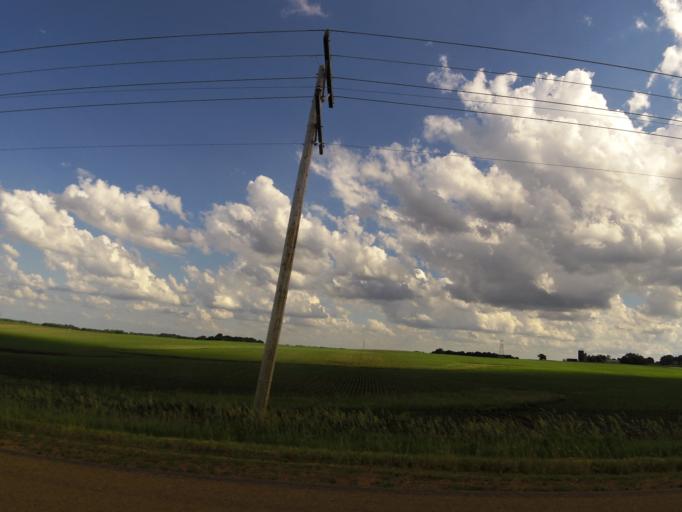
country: US
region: Minnesota
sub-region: Carver County
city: Victoria
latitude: 44.8189
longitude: -93.7121
